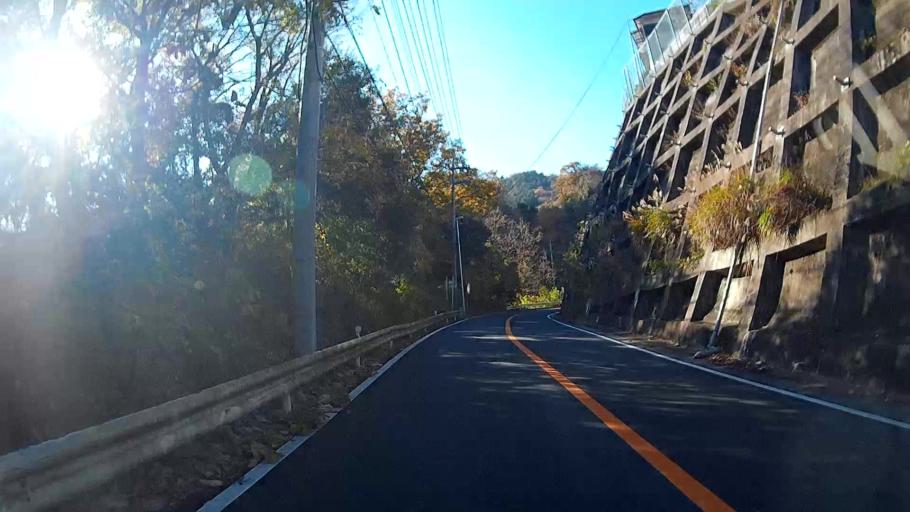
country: JP
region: Yamanashi
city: Uenohara
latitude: 35.6084
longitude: 139.1242
